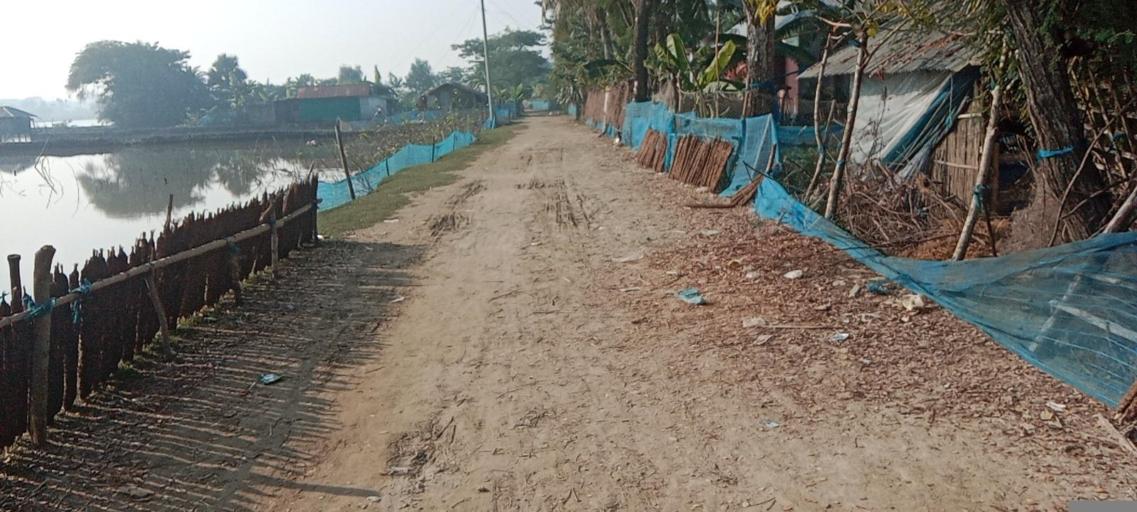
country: BD
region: Khulna
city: Phultala
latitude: 22.6093
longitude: 89.5881
